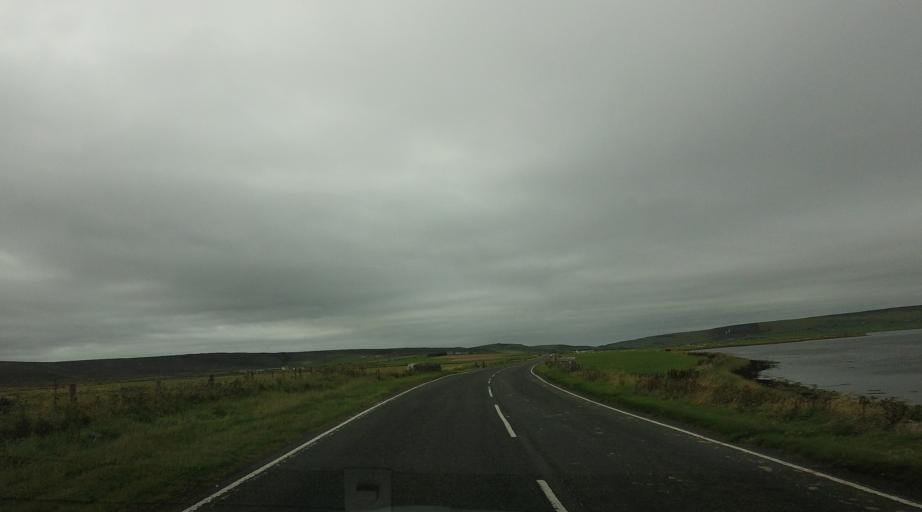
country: GB
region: Scotland
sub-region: Orkney Islands
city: Orkney
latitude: 58.9935
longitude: -3.0550
